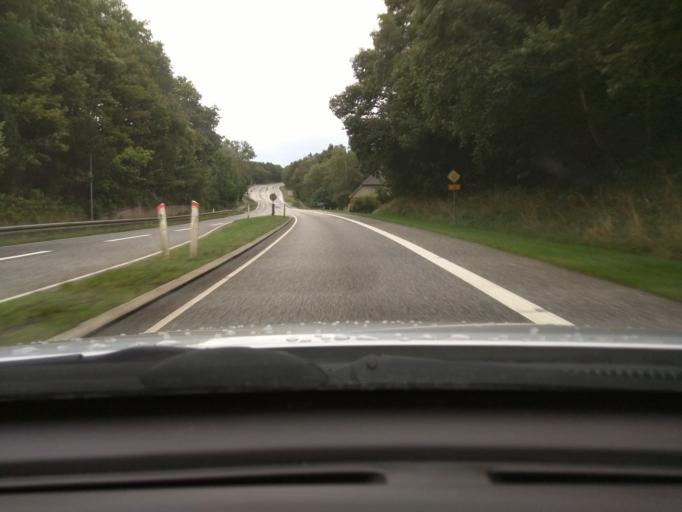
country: DK
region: Central Jutland
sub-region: Viborg Kommune
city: Viborg
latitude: 56.4018
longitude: 9.3715
